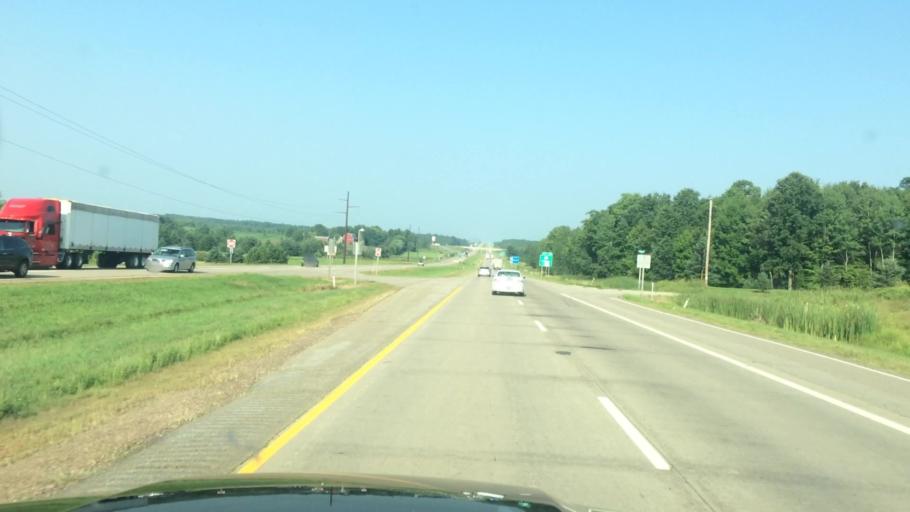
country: US
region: Wisconsin
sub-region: Marathon County
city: Edgar
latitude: 44.9446
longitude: -89.9449
